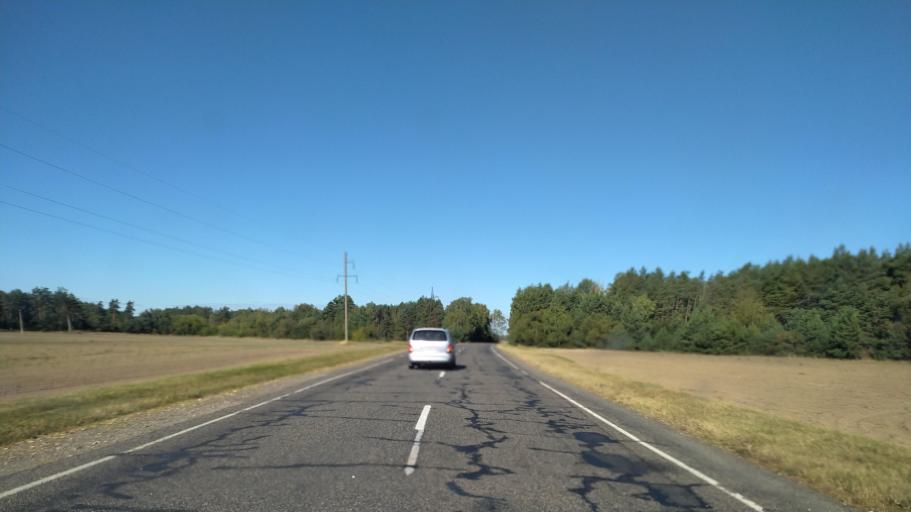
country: BY
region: Brest
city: Byaroza
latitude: 52.4898
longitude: 24.7323
